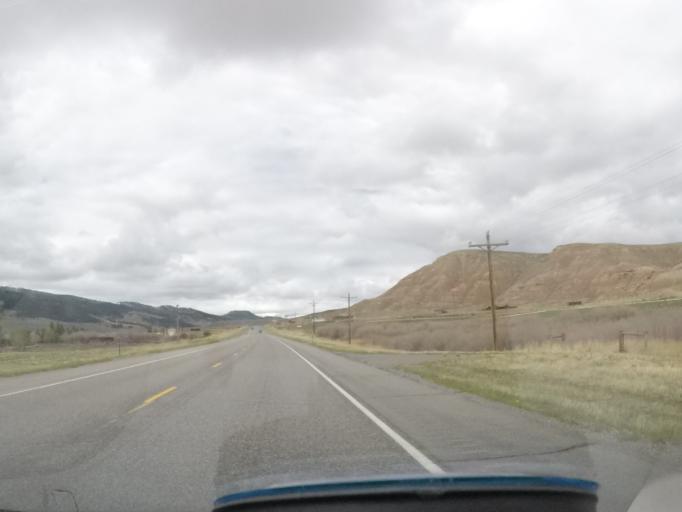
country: US
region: Wyoming
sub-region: Sublette County
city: Pinedale
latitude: 43.5680
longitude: -109.7105
